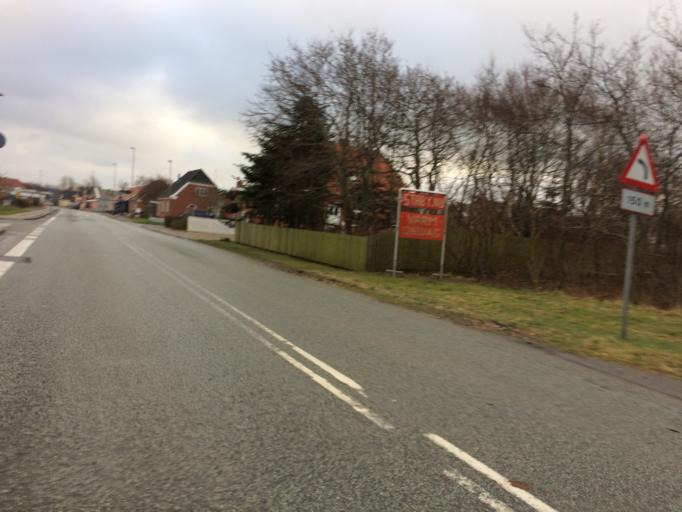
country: DK
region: Central Jutland
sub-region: Holstebro Kommune
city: Ulfborg
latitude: 56.2661
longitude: 8.2384
